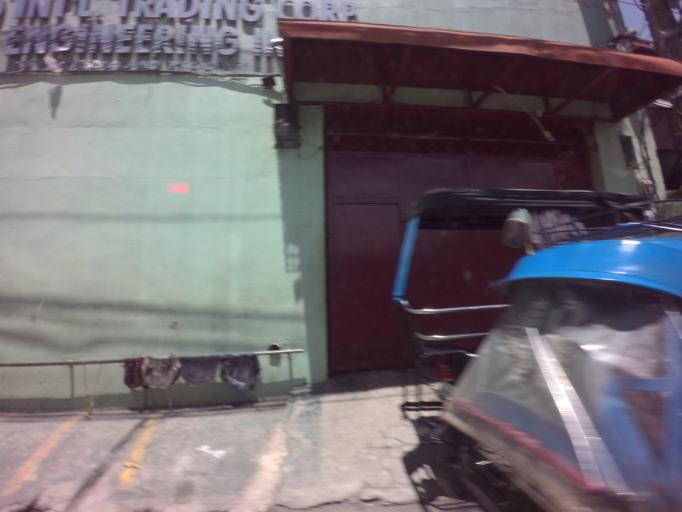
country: PH
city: Sambayanihan People's Village
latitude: 14.4921
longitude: 120.9896
